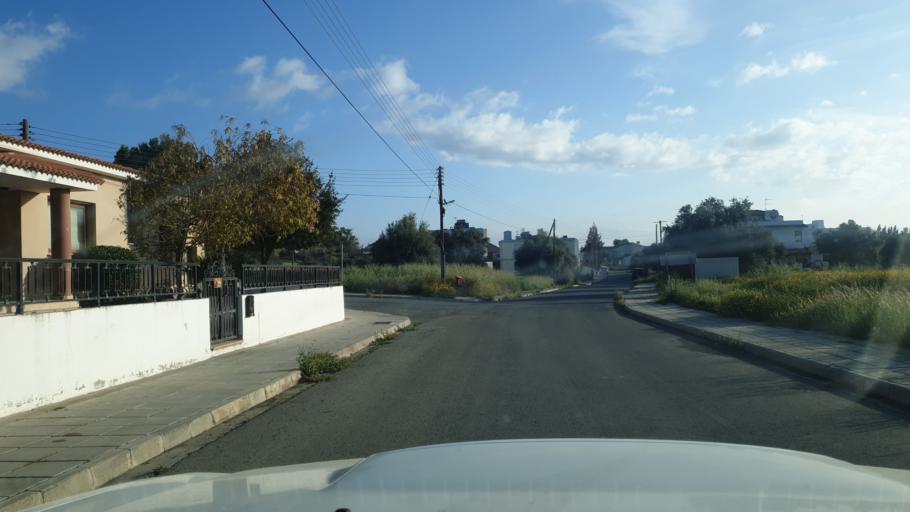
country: CY
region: Lefkosia
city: Tseri
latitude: 35.0675
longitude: 33.3198
